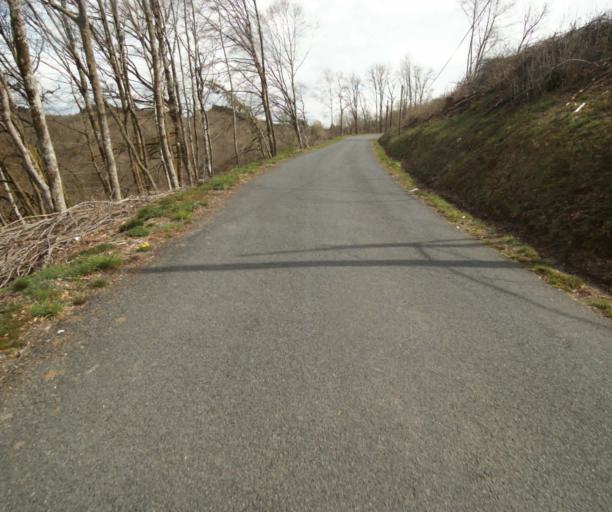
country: FR
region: Limousin
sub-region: Departement de la Correze
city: Correze
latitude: 45.3795
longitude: 1.8980
